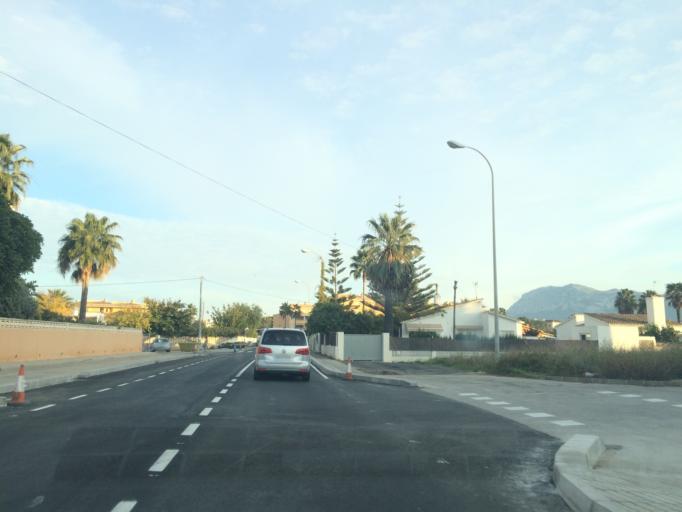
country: ES
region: Valencia
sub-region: Provincia de Alicante
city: Denia
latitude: 38.8571
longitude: 0.0664
